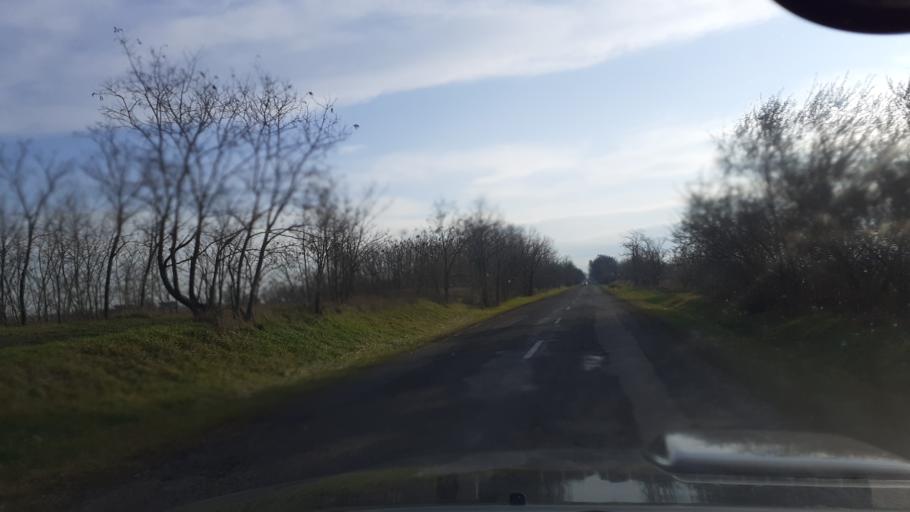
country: HU
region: Pest
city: Domsod
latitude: 47.1024
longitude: 19.0916
